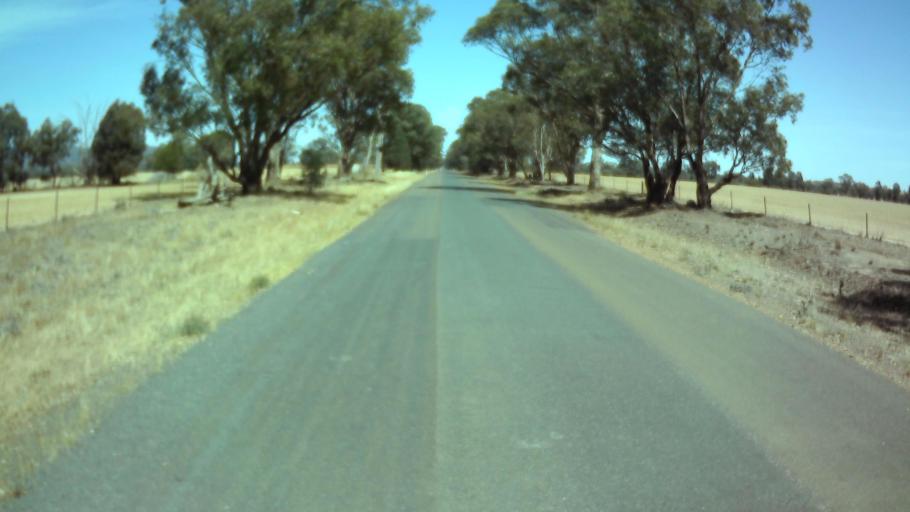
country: AU
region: New South Wales
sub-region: Weddin
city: Grenfell
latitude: -33.8669
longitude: 148.0598
